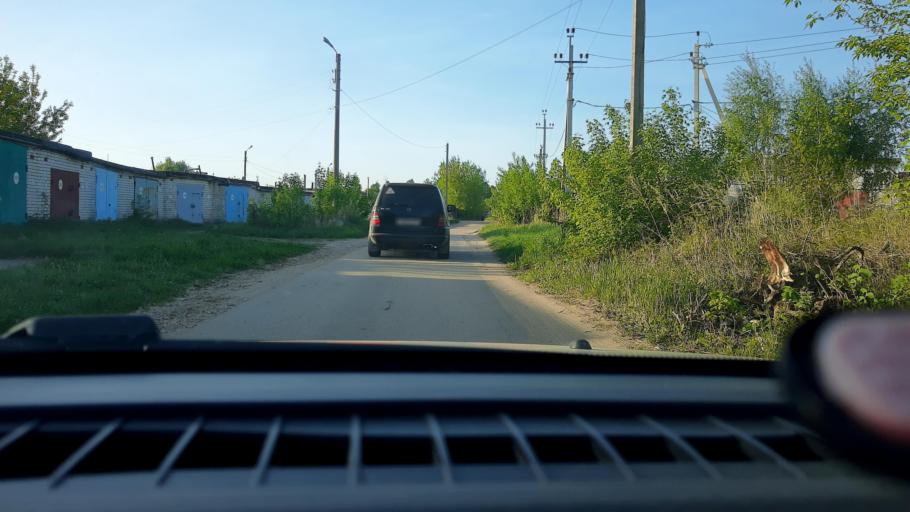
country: RU
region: Nizjnij Novgorod
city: Kstovo
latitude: 56.1334
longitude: 44.1912
